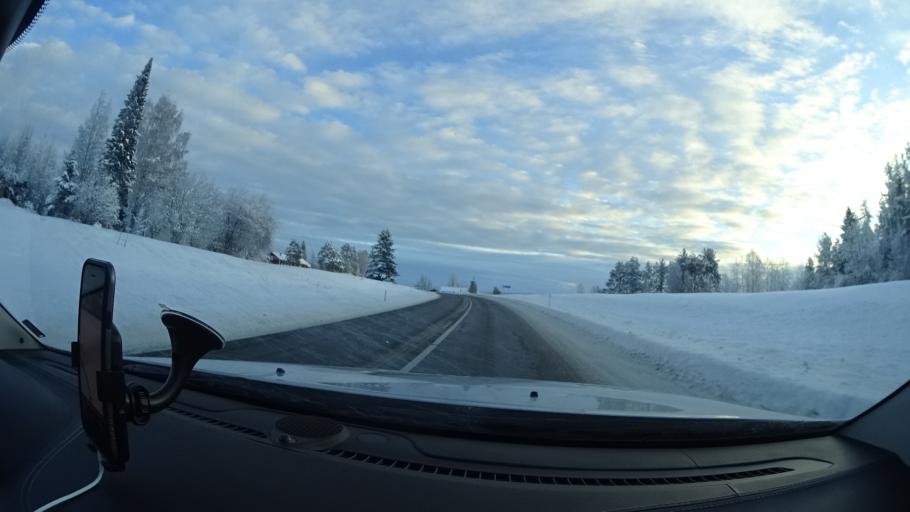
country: SE
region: Jaemtland
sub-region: Ragunda Kommun
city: Hammarstrand
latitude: 63.0363
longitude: 16.5529
